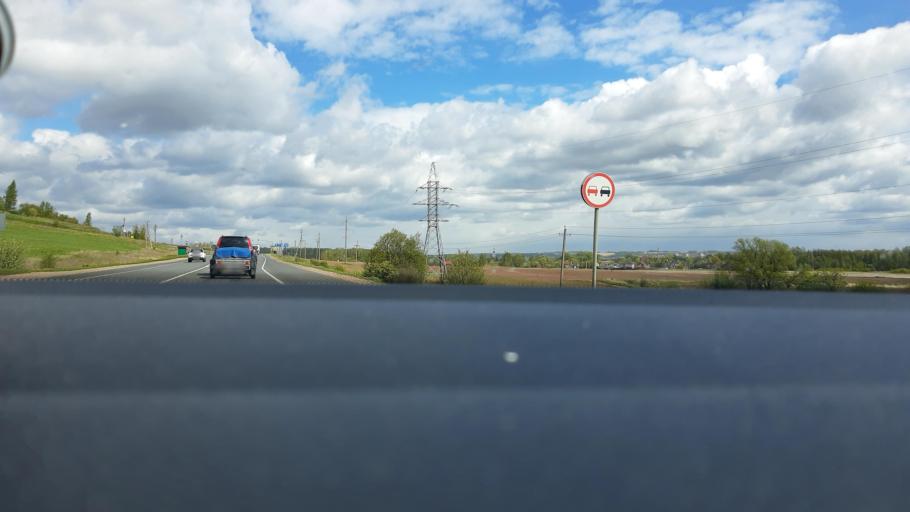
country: RU
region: Moskovskaya
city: Dmitrov
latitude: 56.3414
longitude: 37.4833
